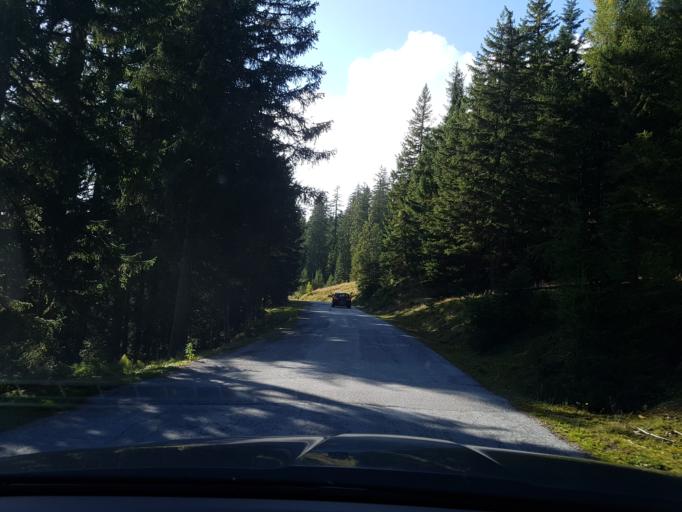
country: AT
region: Salzburg
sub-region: Politischer Bezirk Sankt Johann im Pongau
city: Filzmoos
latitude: 47.4099
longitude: 13.5023
